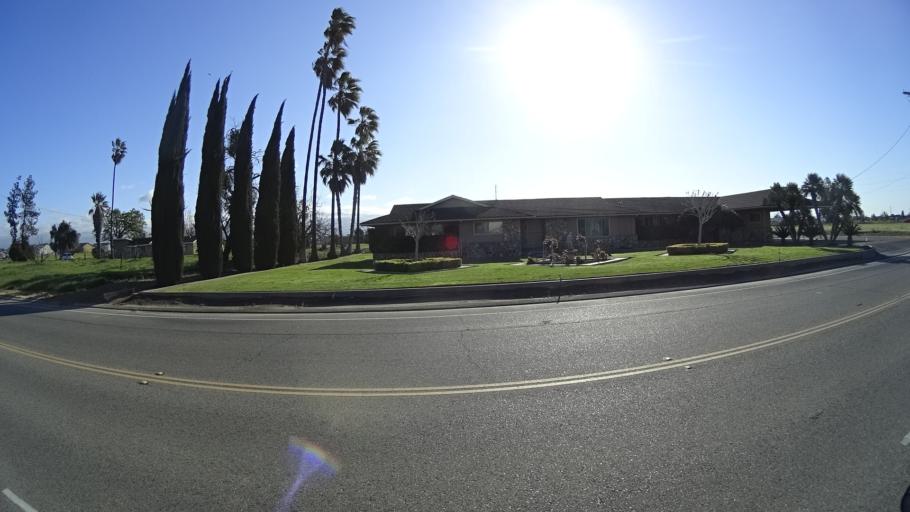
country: US
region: California
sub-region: Fresno County
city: West Park
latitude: 36.7947
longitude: -119.9074
